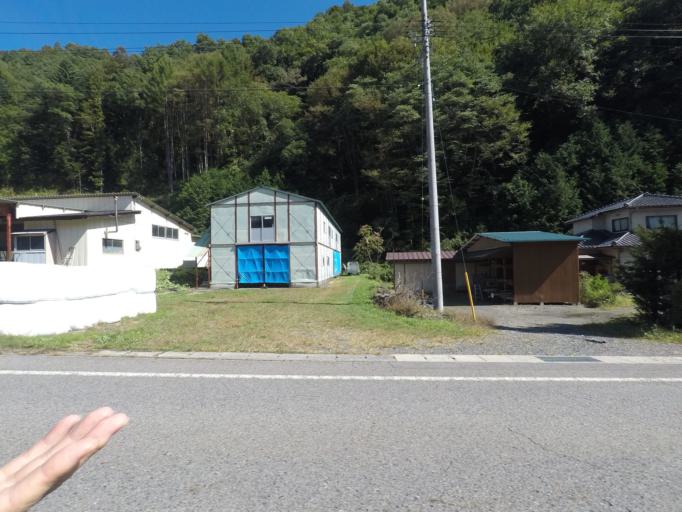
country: JP
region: Nagano
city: Tatsuno
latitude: 35.9788
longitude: 137.7474
